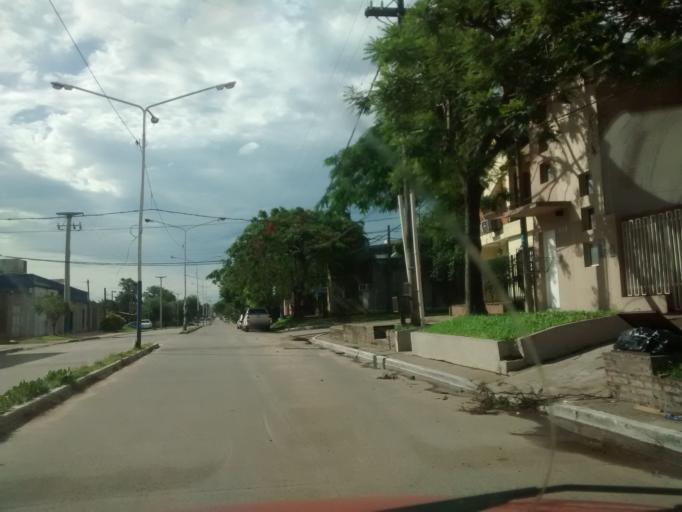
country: AR
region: Chaco
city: Resistencia
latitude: -27.4378
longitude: -58.9871
